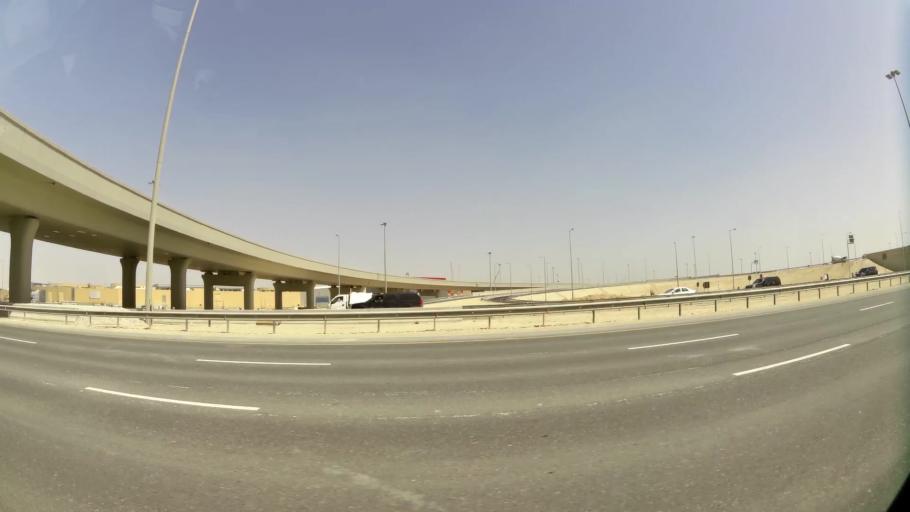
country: QA
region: Baladiyat Umm Salal
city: Umm Salal Muhammad
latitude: 25.3806
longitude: 51.4396
